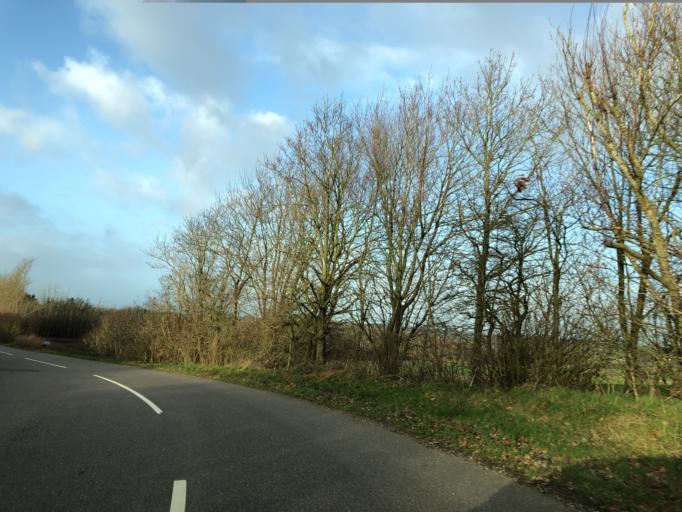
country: DK
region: Central Jutland
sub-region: Ringkobing-Skjern Kommune
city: Videbaek
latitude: 56.1893
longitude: 8.5447
